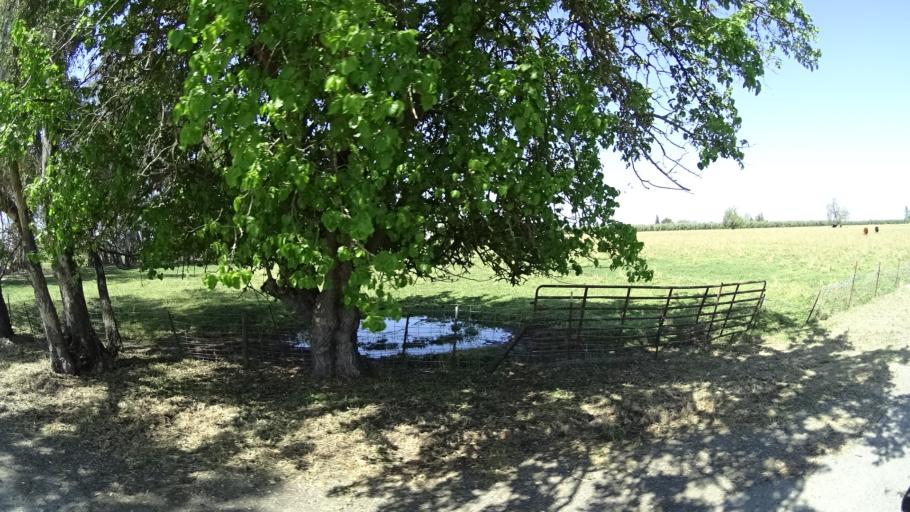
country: US
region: California
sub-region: Glenn County
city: Orland
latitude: 39.7655
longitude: -122.1617
